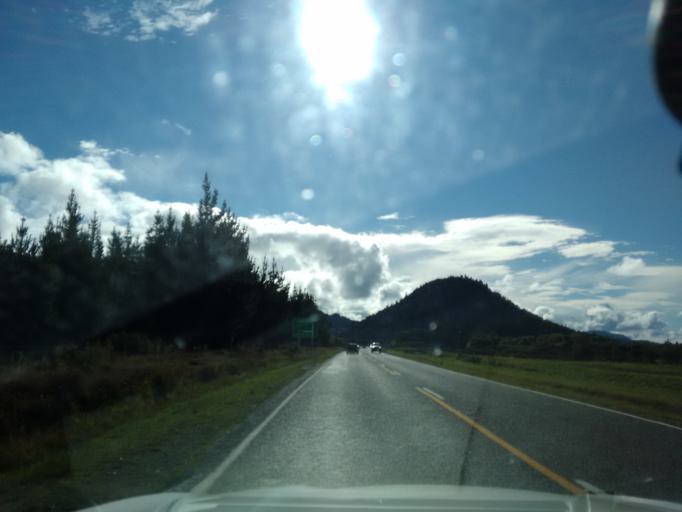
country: NZ
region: Waikato
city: Turangi
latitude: -38.9834
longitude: 175.7817
